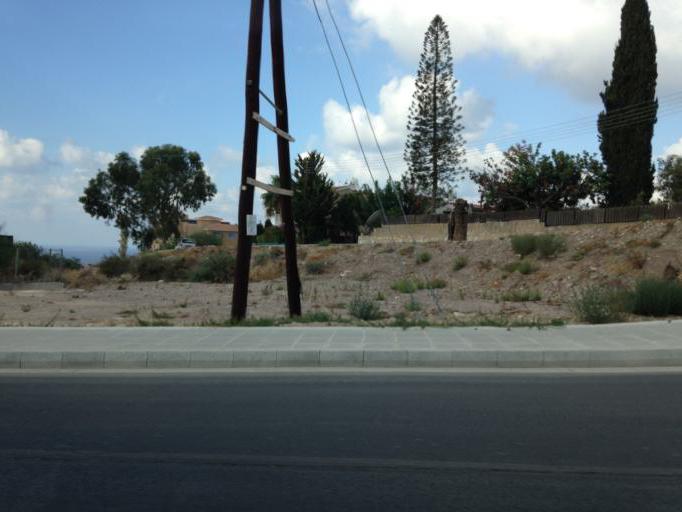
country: CY
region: Pafos
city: Pegeia
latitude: 34.8770
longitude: 32.3805
